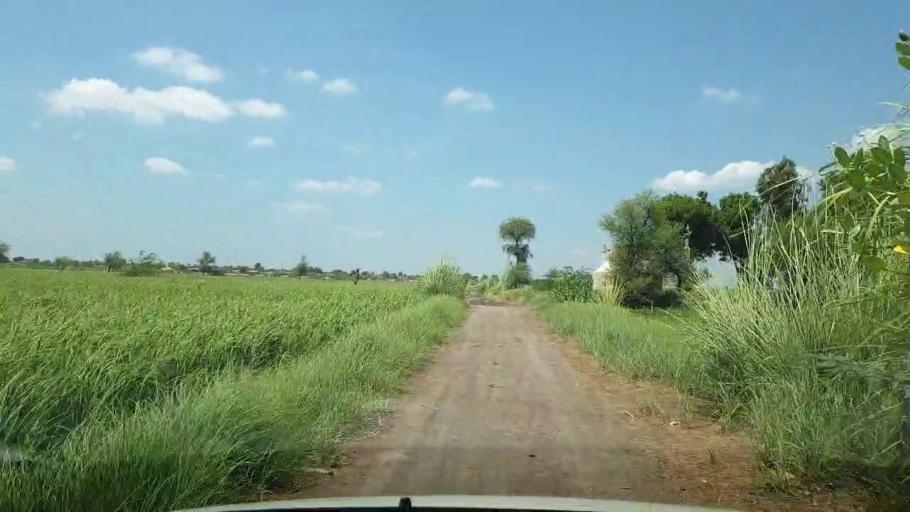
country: PK
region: Sindh
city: Sanghar
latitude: 26.0729
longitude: 69.0479
